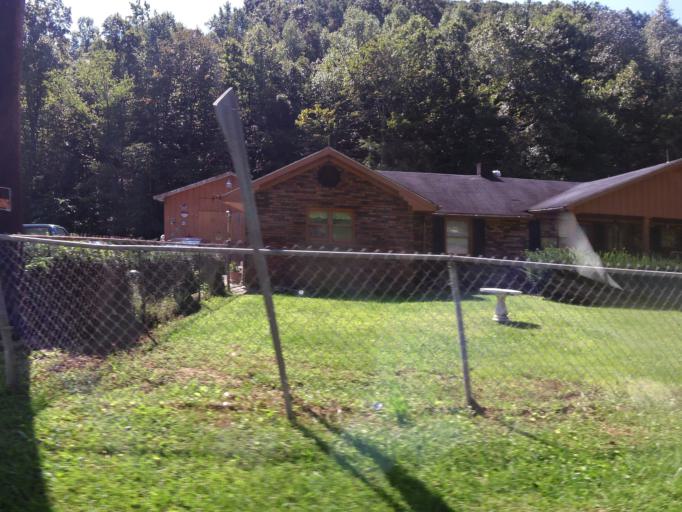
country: US
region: Kentucky
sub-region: Clay County
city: Manchester
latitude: 37.0859
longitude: -83.6848
